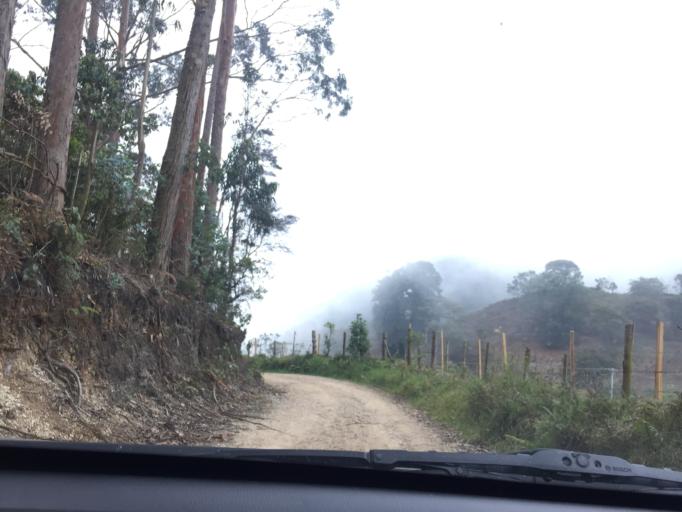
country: CO
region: Cundinamarca
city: Bojaca
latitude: 4.7049
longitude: -74.3626
